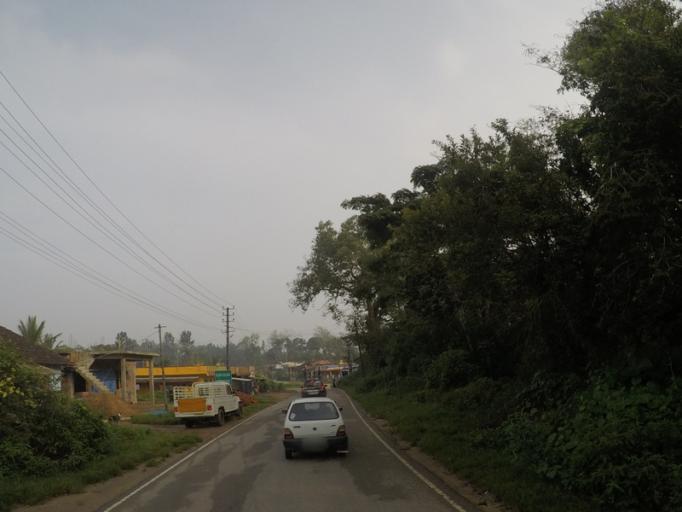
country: IN
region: Karnataka
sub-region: Chikmagalur
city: Mudigere
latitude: 13.2498
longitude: 75.6416
